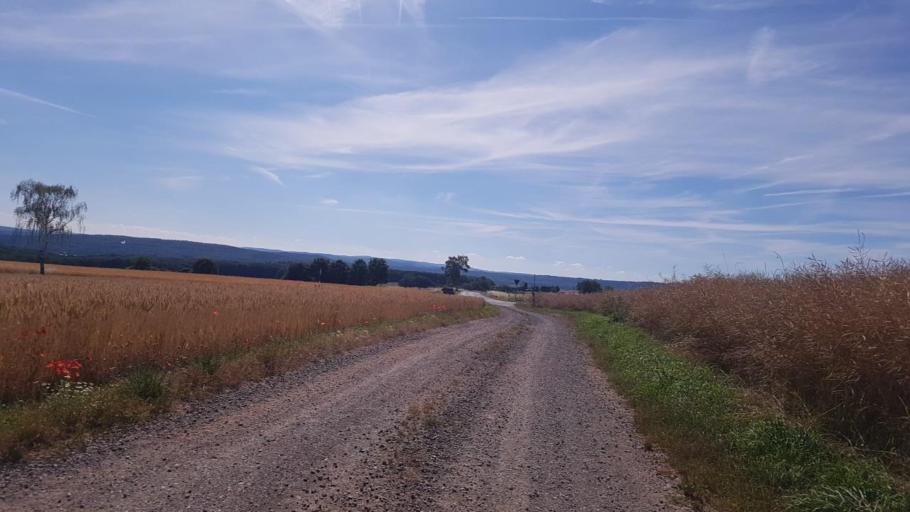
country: DE
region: North Rhine-Westphalia
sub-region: Regierungsbezirk Koln
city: Kall
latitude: 50.6175
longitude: 6.5589
